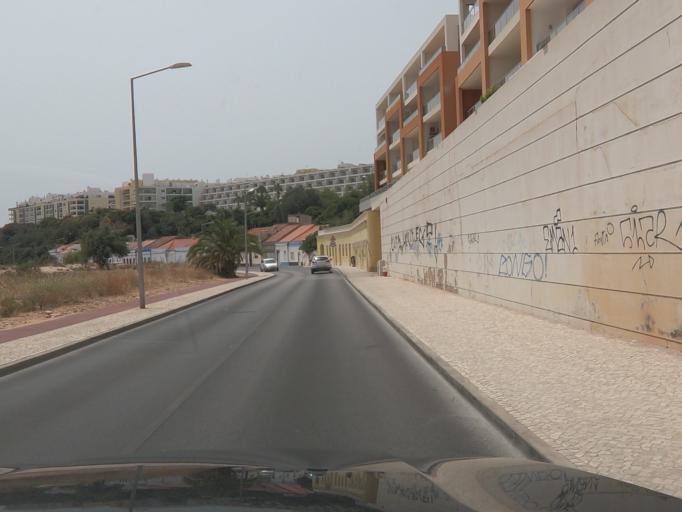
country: PT
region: Faro
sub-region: Portimao
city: Portimao
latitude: 37.1275
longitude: -8.5341
